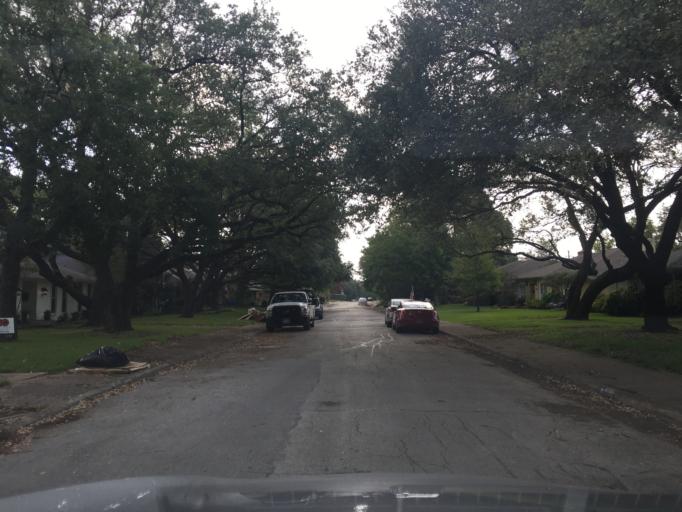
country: US
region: Texas
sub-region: Dallas County
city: Richardson
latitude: 32.8969
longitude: -96.7409
